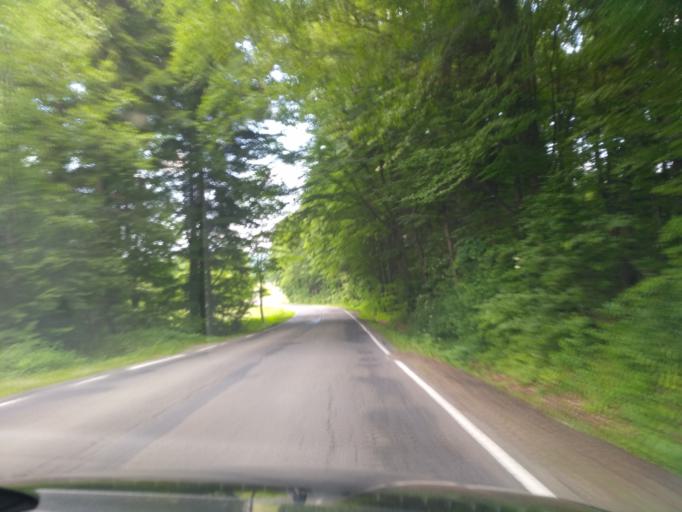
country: PL
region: Subcarpathian Voivodeship
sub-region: Powiat rzeszowski
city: Hyzne
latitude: 49.9434
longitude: 22.1901
